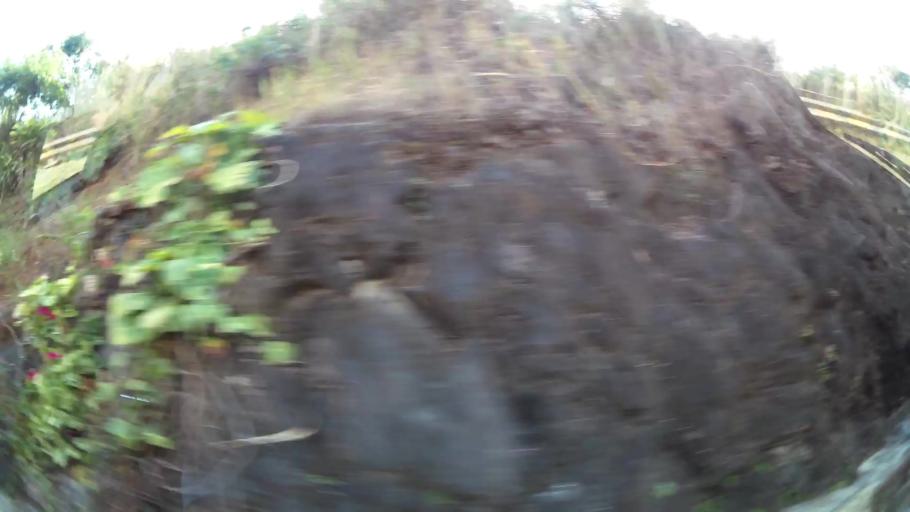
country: CO
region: Valle del Cauca
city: Cali
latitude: 3.4347
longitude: -76.5571
